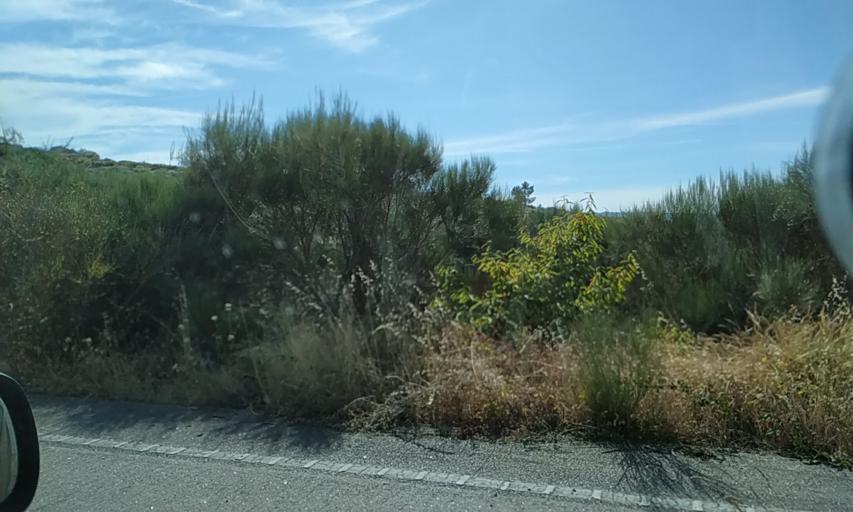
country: PT
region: Vila Real
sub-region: Murca
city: Murca
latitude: 41.3715
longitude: -7.5512
